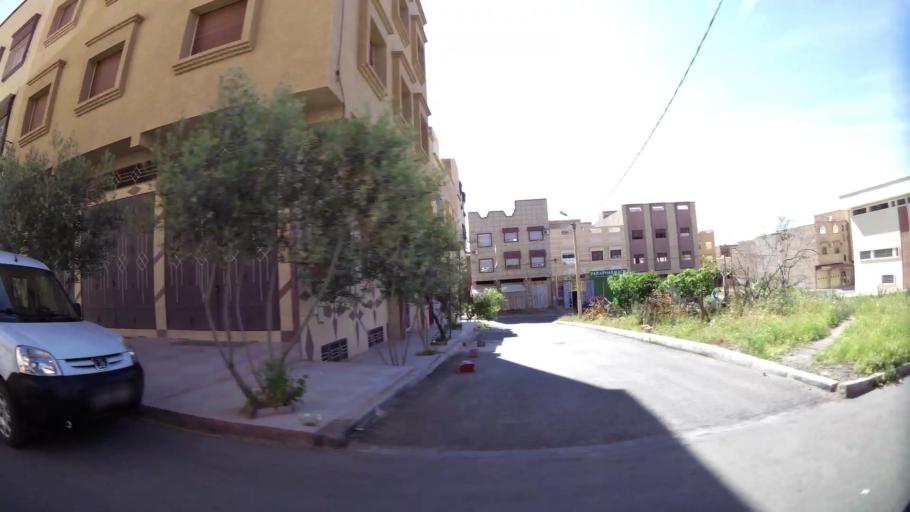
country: MA
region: Oriental
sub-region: Oujda-Angad
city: Oujda
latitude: 34.6580
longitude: -1.9142
